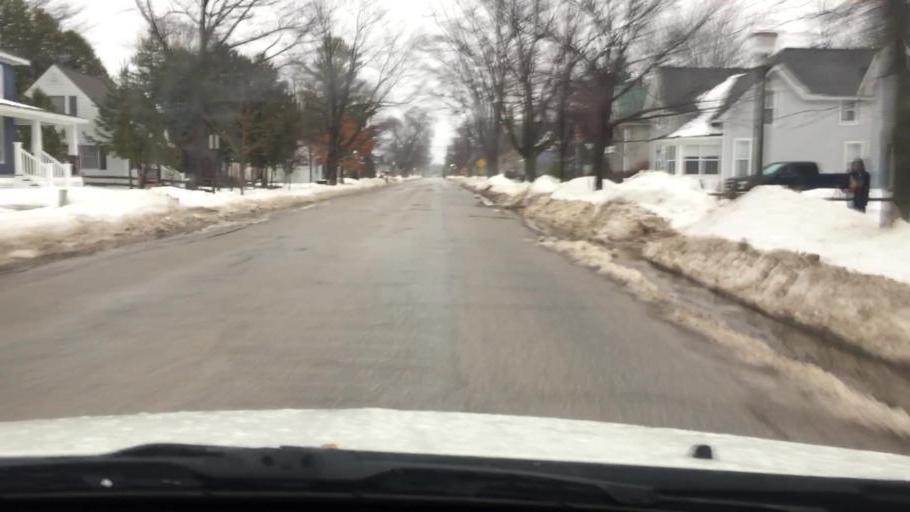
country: US
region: Michigan
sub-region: Charlevoix County
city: Charlevoix
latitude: 45.3153
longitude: -85.2661
